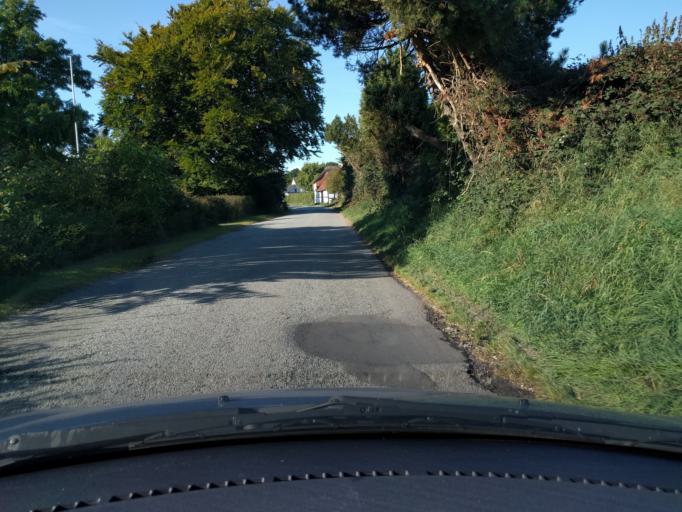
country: DK
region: South Denmark
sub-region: Assens Kommune
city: Harby
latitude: 55.1392
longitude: 10.0243
